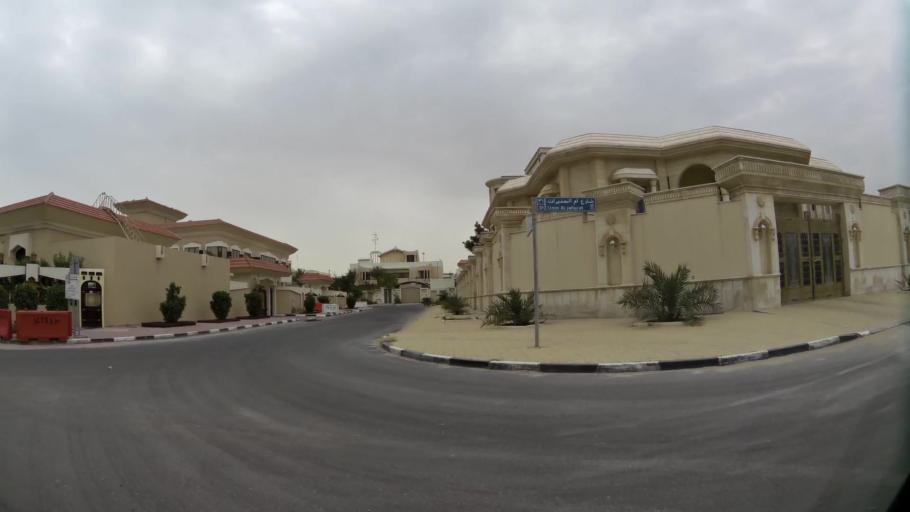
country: QA
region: Baladiyat ar Rayyan
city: Ar Rayyan
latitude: 25.3411
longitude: 51.4624
